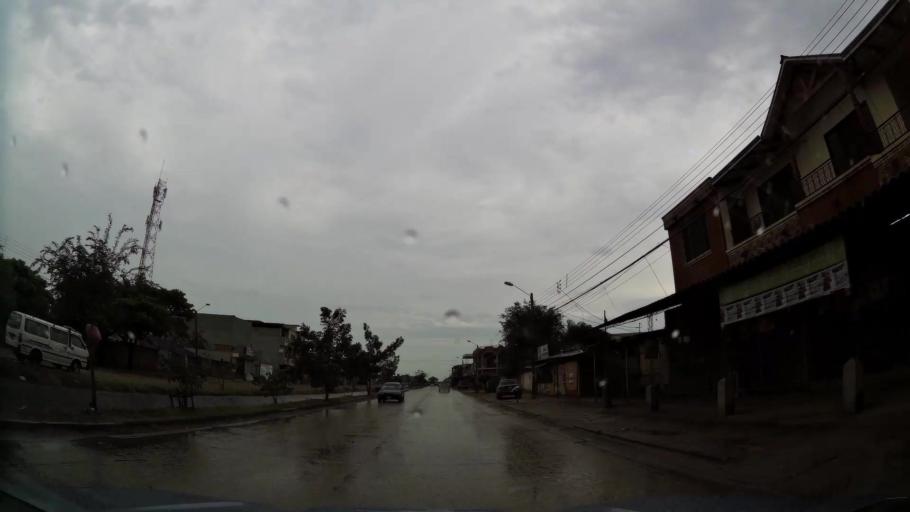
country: BO
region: Santa Cruz
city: Santa Cruz de la Sierra
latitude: -17.8051
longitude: -63.1281
